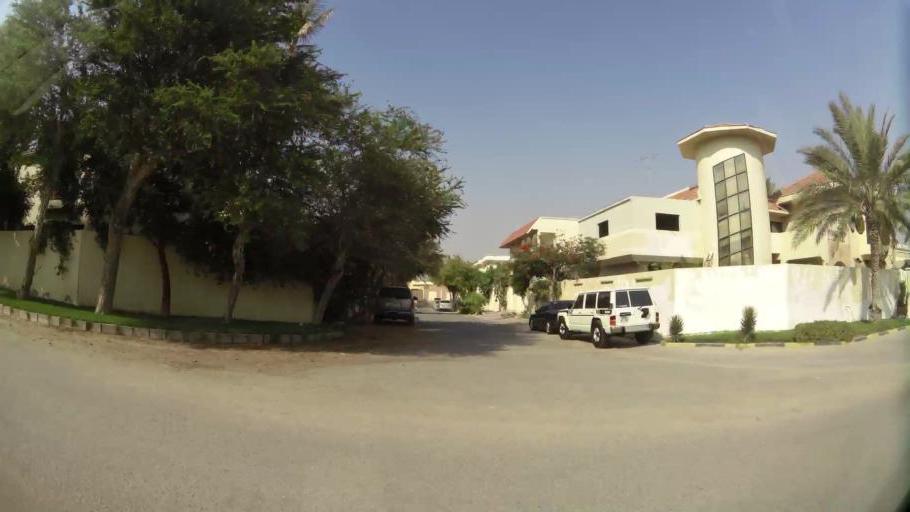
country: AE
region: Ajman
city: Ajman
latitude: 25.3852
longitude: 55.4296
